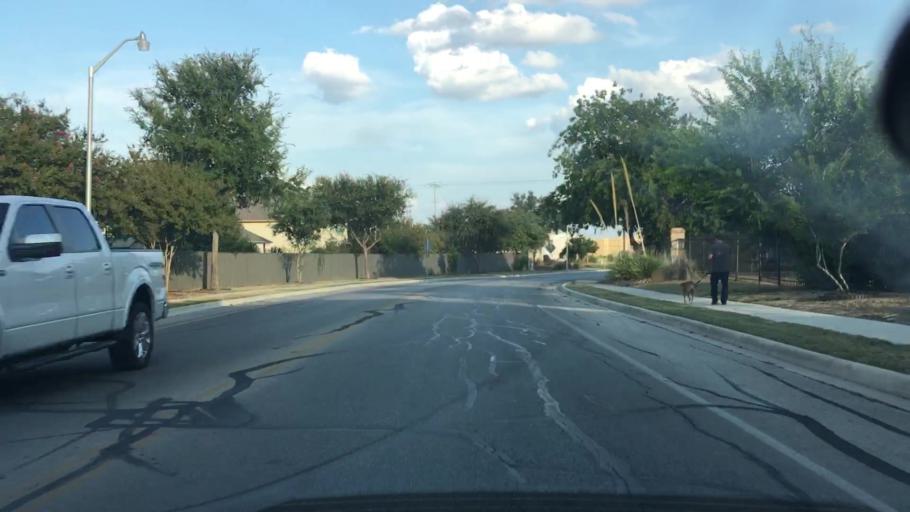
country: US
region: Texas
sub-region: Guadalupe County
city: Cibolo
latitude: 29.5764
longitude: -98.2372
